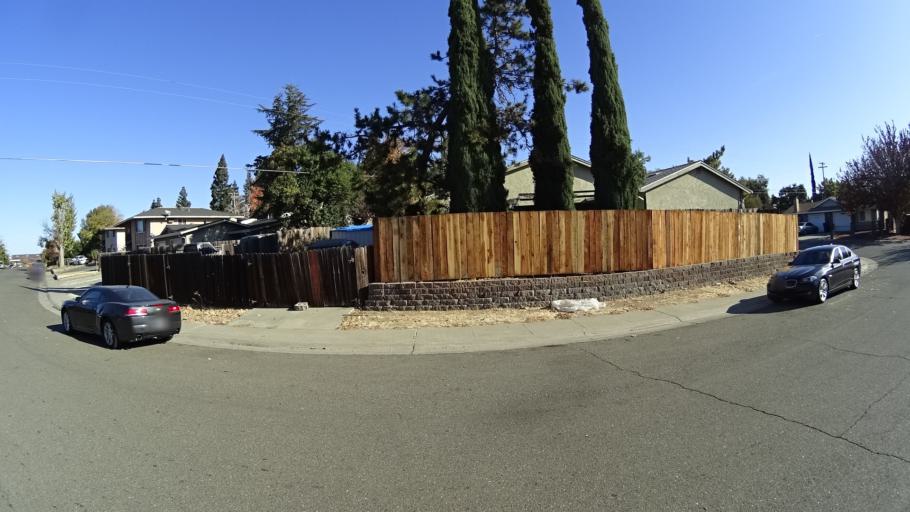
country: US
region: California
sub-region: Sacramento County
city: Citrus Heights
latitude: 38.6760
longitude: -121.2973
